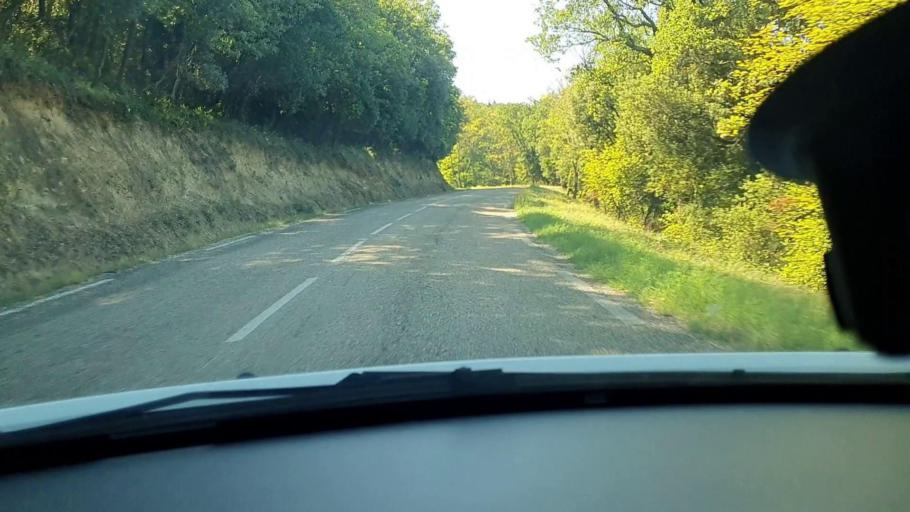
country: FR
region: Languedoc-Roussillon
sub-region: Departement du Gard
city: Saint-Paulet-de-Caisson
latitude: 44.2386
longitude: 4.5616
